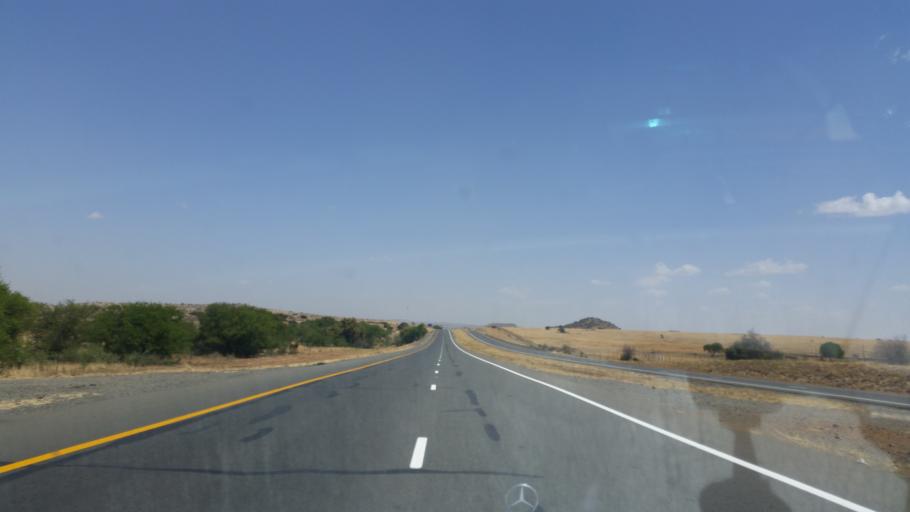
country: ZA
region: Orange Free State
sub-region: Lejweleputswa District Municipality
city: Brandfort
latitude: -28.9218
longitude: 26.4394
